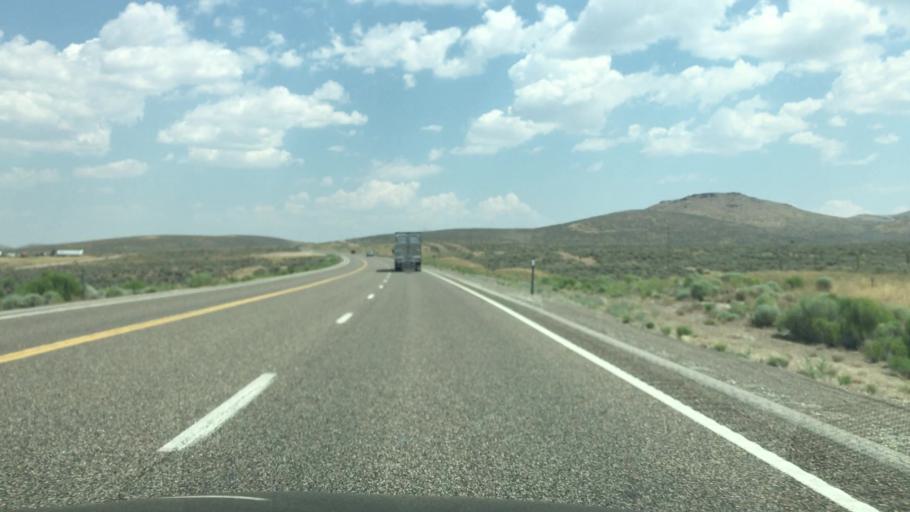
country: US
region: Nevada
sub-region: Elko County
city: Wells
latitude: 41.1747
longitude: -114.8794
